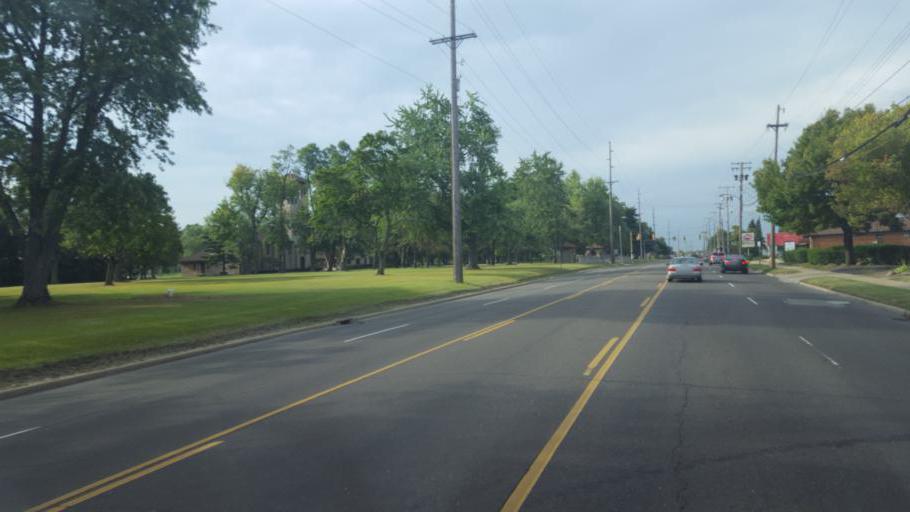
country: US
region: Ohio
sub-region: Mahoning County
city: Youngstown
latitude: 41.1273
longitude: -80.6645
